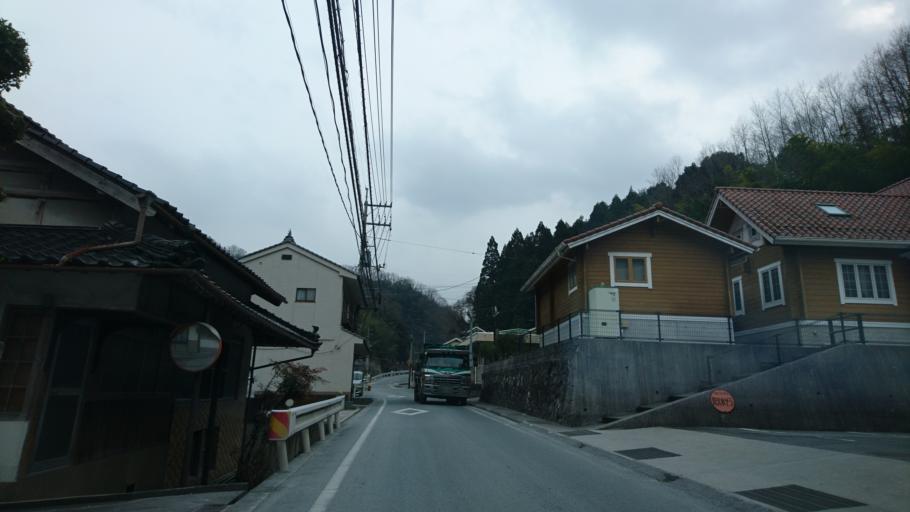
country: JP
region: Okayama
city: Niimi
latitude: 34.9298
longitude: 133.5198
